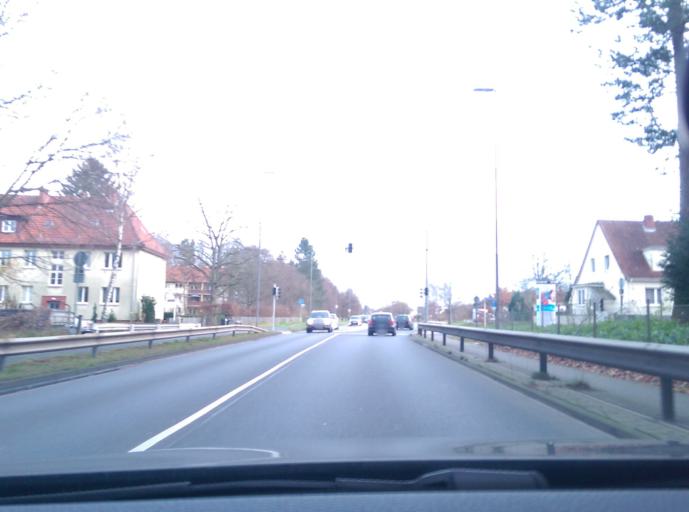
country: DE
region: Lower Saxony
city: Celle
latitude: 52.6096
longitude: 10.0432
